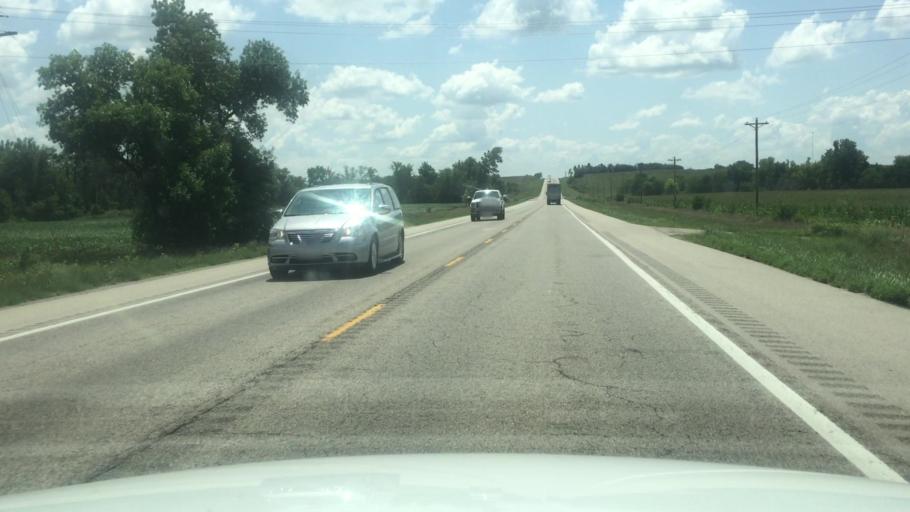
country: US
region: Kansas
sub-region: Brown County
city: Horton
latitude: 39.6864
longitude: -95.7304
